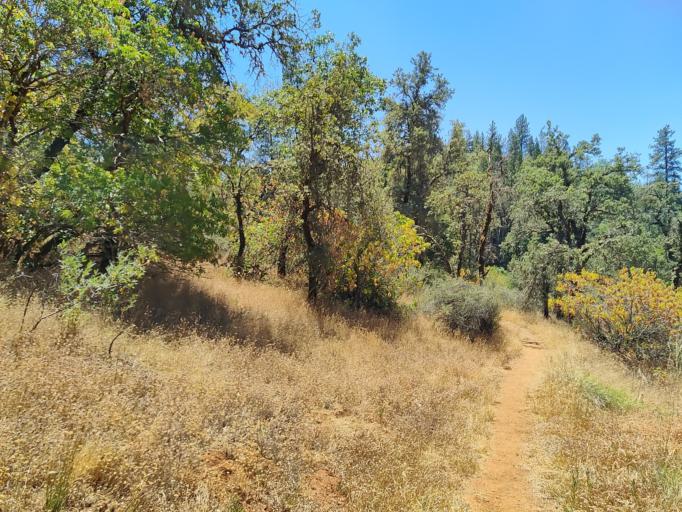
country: US
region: California
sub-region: Placer County
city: Meadow Vista
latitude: 39.0259
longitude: -120.9891
